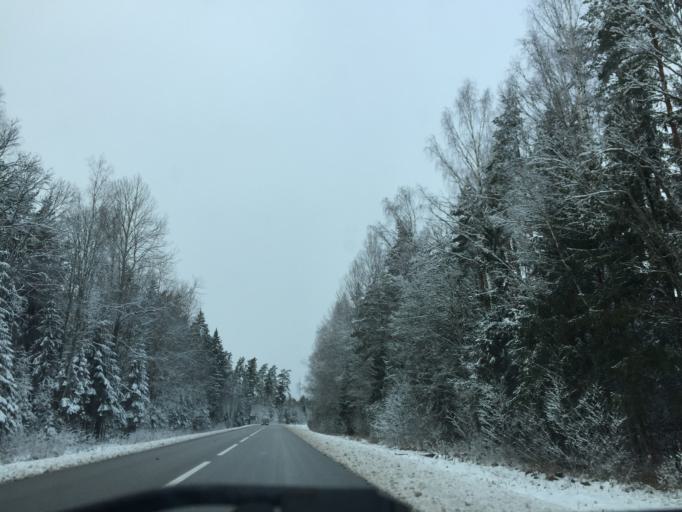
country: LV
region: Kuldigas Rajons
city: Kuldiga
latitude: 57.2679
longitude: 22.0698
